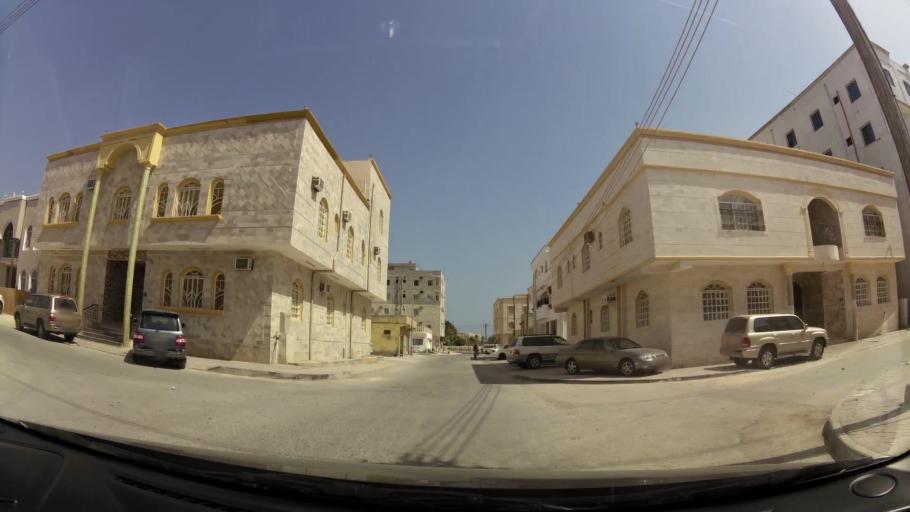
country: OM
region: Zufar
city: Salalah
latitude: 17.0133
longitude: 54.0596
